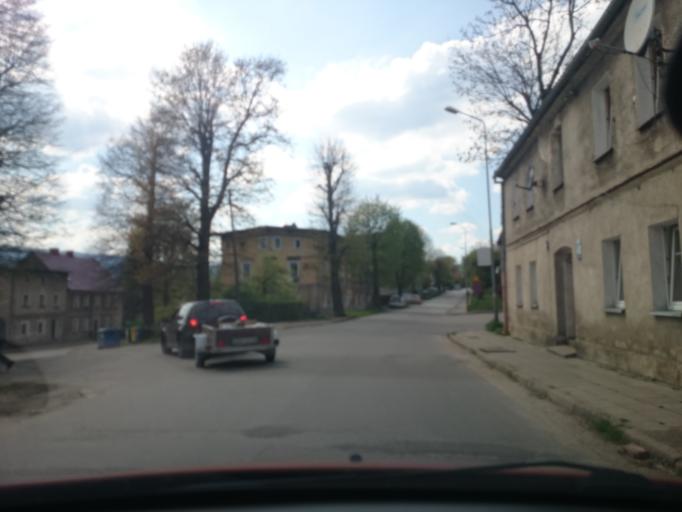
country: PL
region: Lower Silesian Voivodeship
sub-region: Powiat klodzki
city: Bystrzyca Klodzka
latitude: 50.2989
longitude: 16.6445
